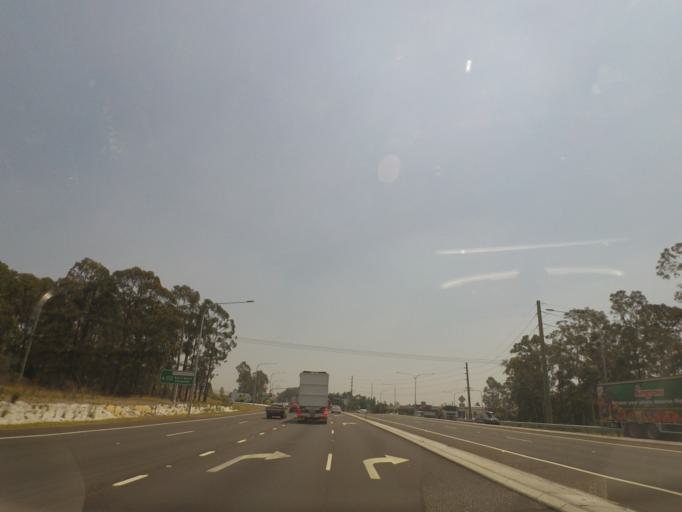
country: AU
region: New South Wales
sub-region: Newcastle
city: Beresfield
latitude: -32.8150
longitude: 151.6357
